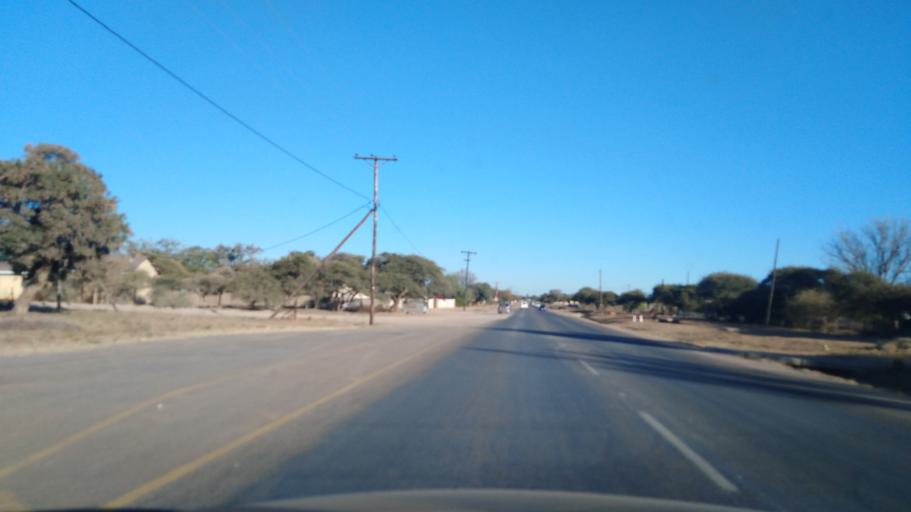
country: BW
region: Central
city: Mahalapye
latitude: -23.0903
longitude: 26.8257
